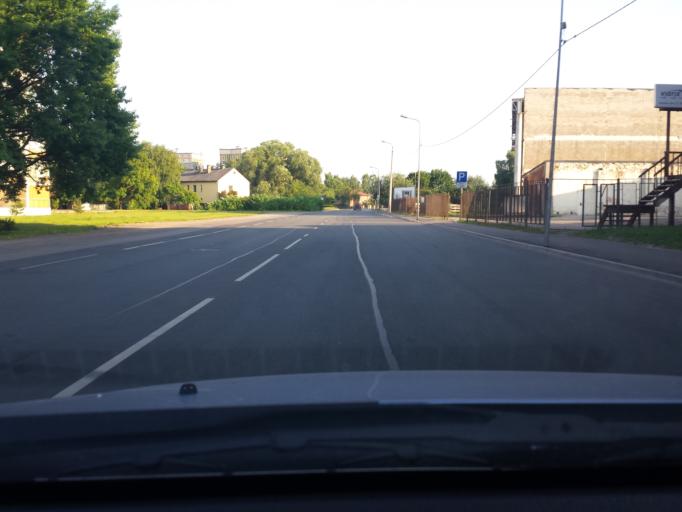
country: LV
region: Riga
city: Riga
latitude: 56.9580
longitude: 24.1655
